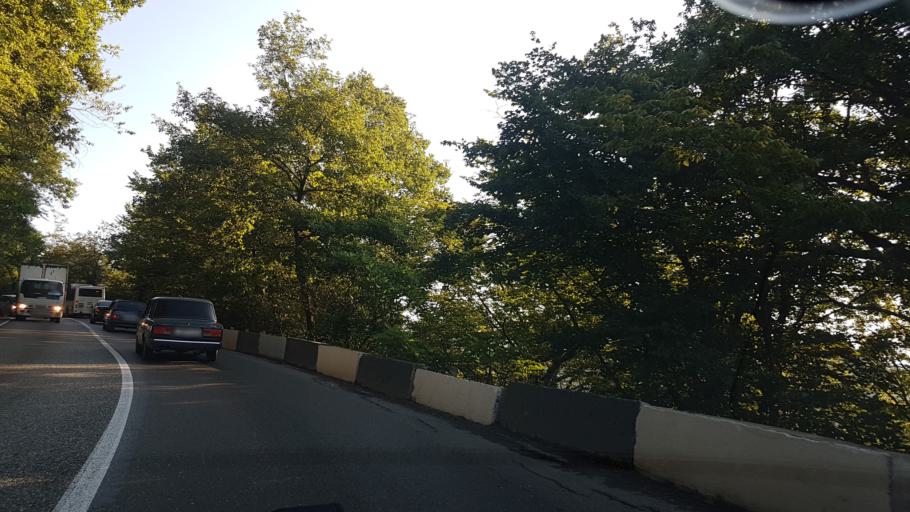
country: RU
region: Krasnodarskiy
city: Dagomys
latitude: 43.6583
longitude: 39.6472
